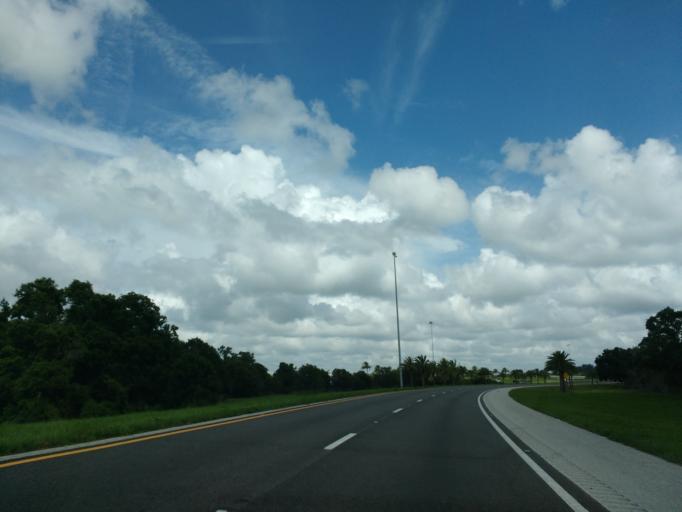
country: US
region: Florida
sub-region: Manatee County
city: Ellenton
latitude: 27.5840
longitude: -82.5171
